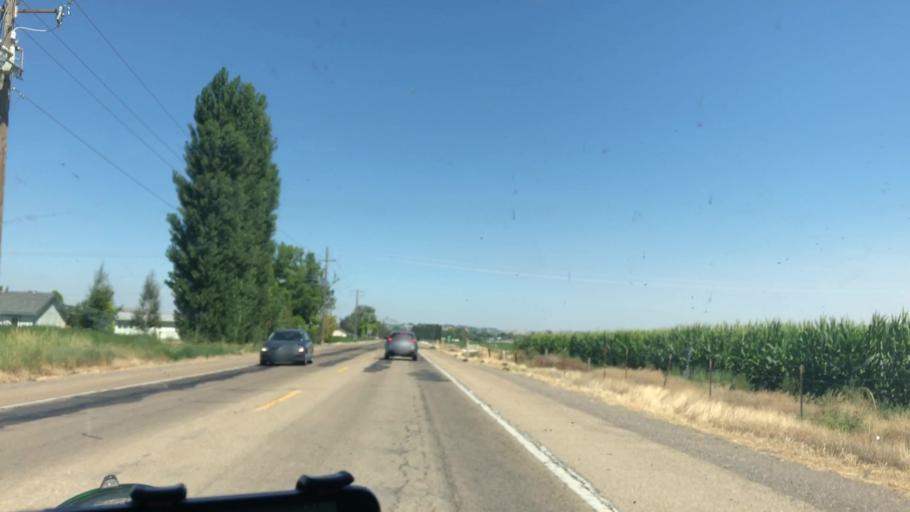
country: US
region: Idaho
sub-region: Owyhee County
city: Marsing
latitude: 43.5453
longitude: -116.8334
